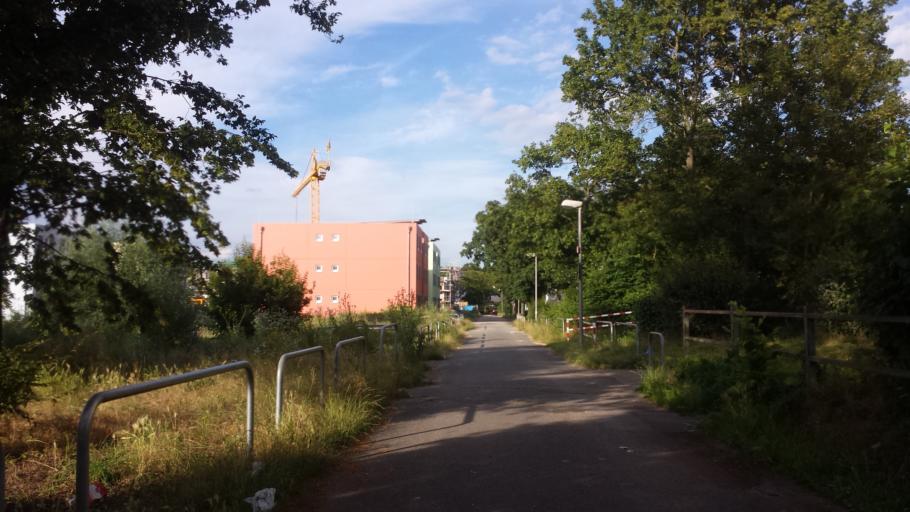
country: DE
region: Rheinland-Pfalz
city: Gartenstadt
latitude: 49.4550
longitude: 8.4189
